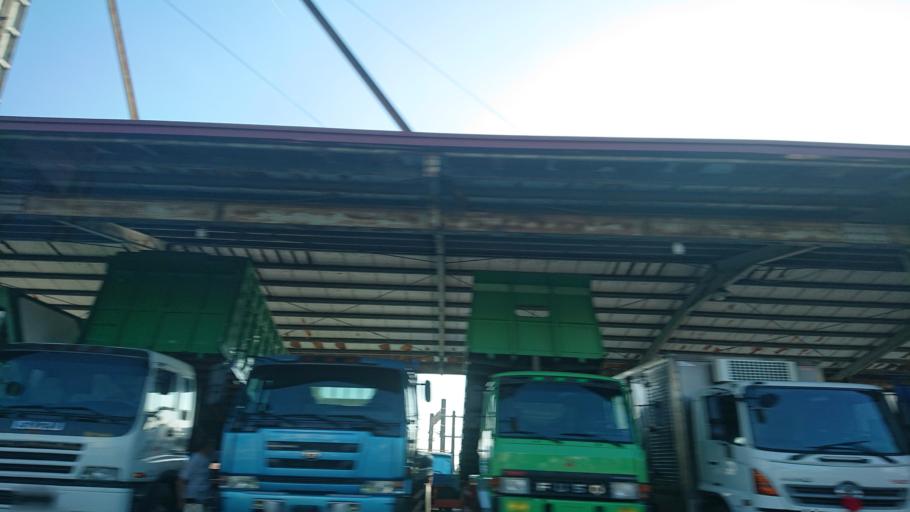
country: TW
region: Taiwan
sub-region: Changhua
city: Chang-hua
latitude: 24.1201
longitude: 120.5728
